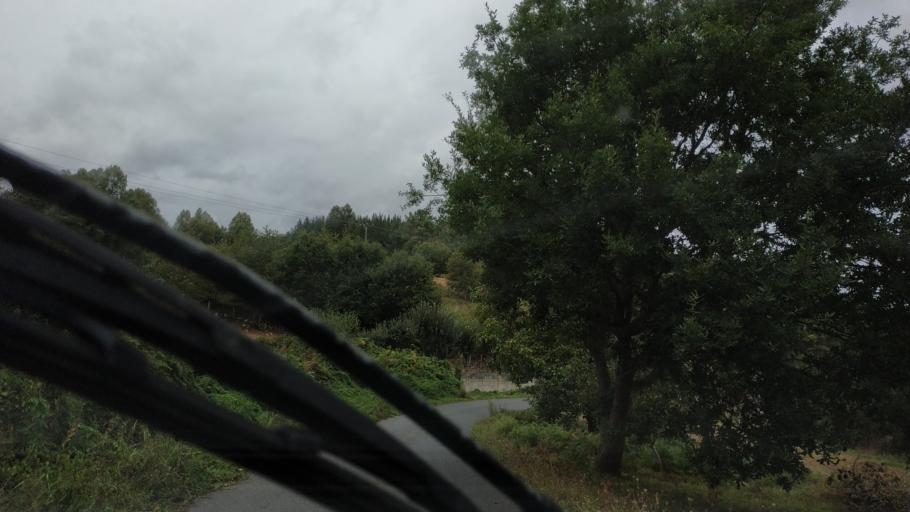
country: ES
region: Galicia
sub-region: Provincia de Lugo
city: Lugo
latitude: 42.9955
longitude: -7.5751
